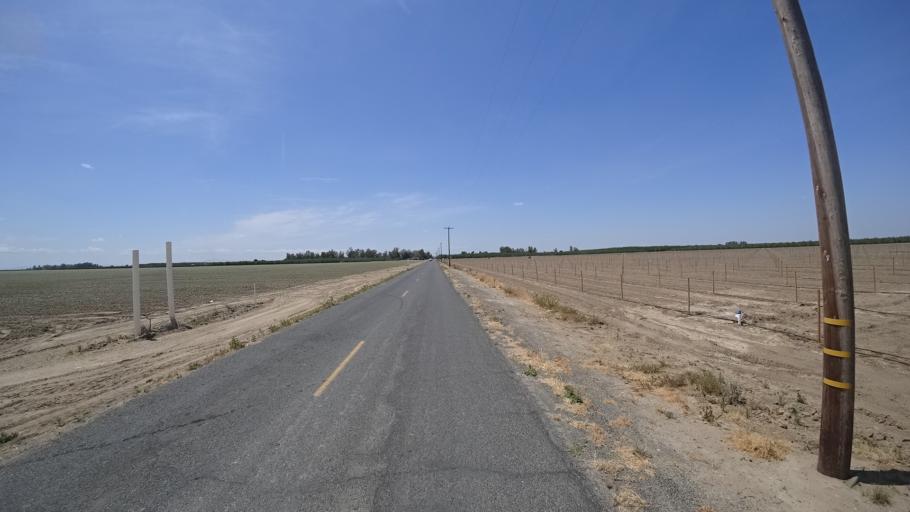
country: US
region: California
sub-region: Kings County
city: Home Garden
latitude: 36.2837
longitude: -119.6568
